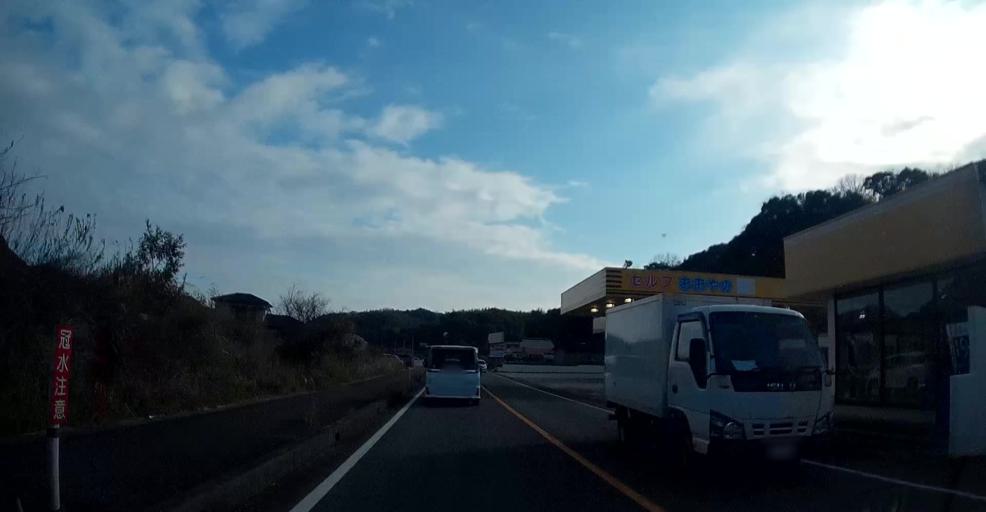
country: JP
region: Kumamoto
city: Yatsushiro
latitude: 32.5664
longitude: 130.4088
